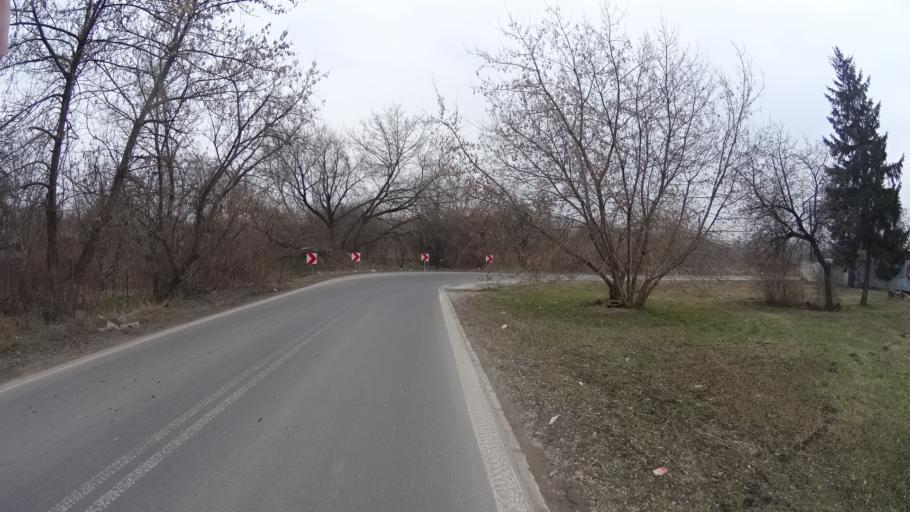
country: PL
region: Masovian Voivodeship
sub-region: Warszawa
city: Wlochy
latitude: 52.2195
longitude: 20.9431
